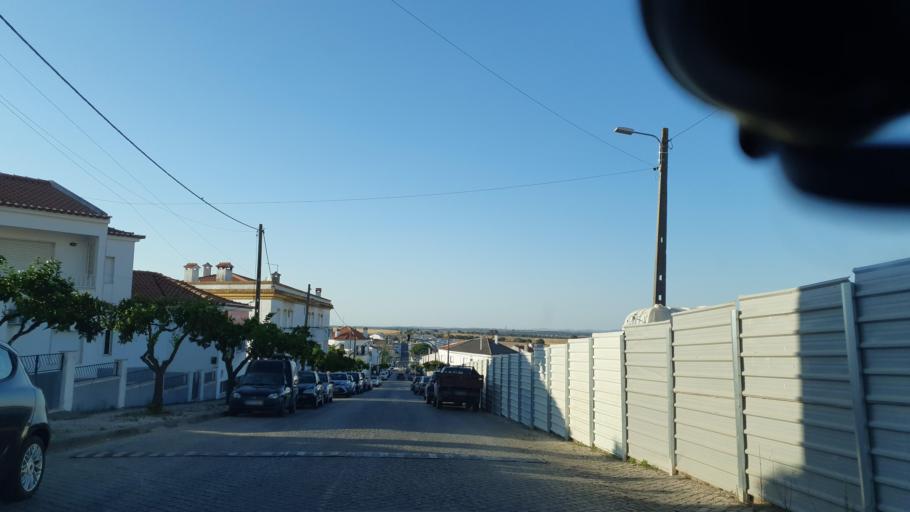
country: PT
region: Portalegre
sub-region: Fronteira
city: Fronteira
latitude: 38.9538
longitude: -7.6742
